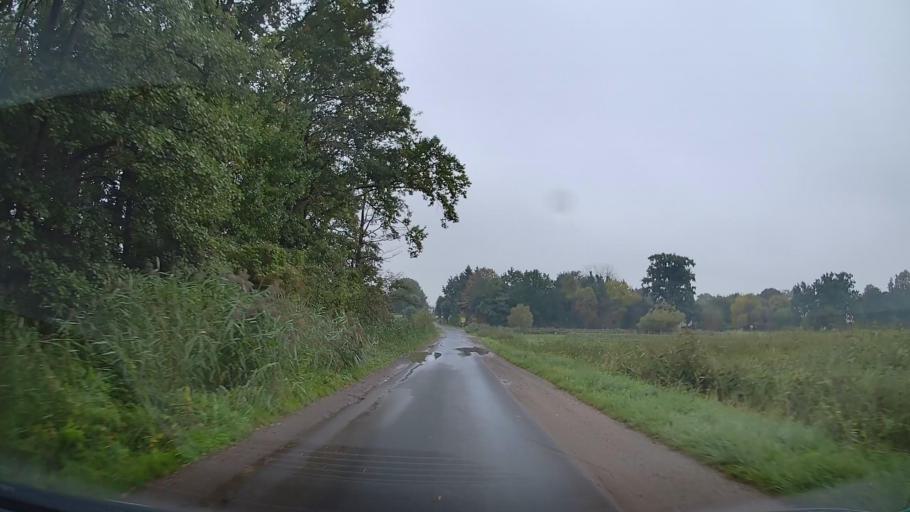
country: DE
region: Mecklenburg-Vorpommern
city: Gramkow
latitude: 53.9284
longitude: 11.3676
